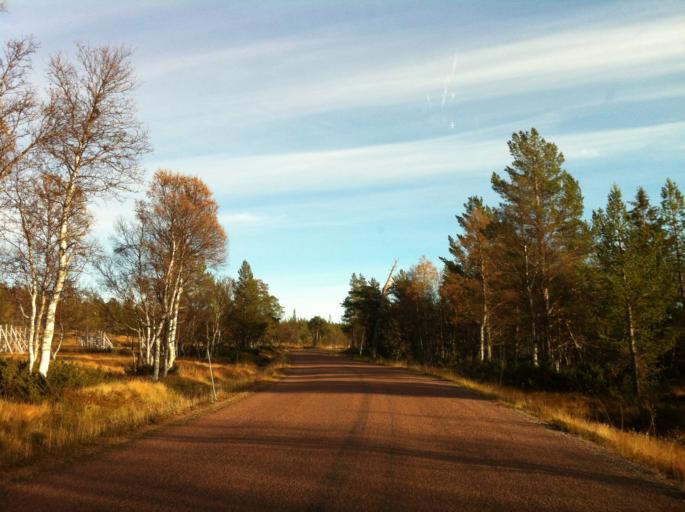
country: NO
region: Hedmark
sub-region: Engerdal
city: Engerdal
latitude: 62.0800
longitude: 12.1544
